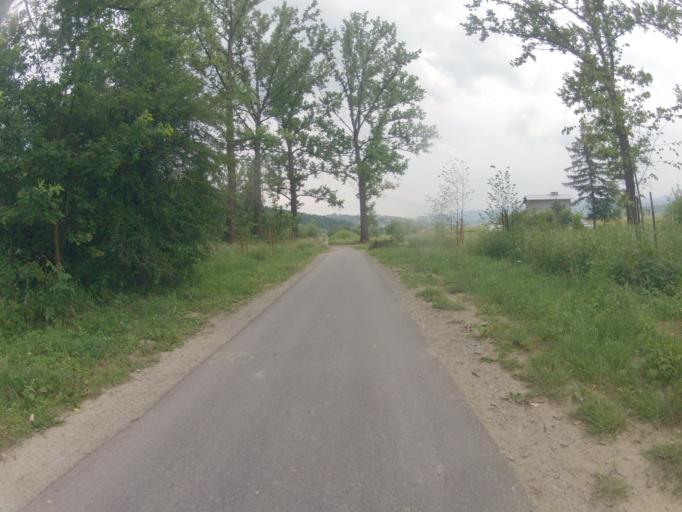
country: PL
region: Lesser Poland Voivodeship
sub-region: Powiat nowosadecki
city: Stary Sacz
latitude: 49.5353
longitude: 20.6598
